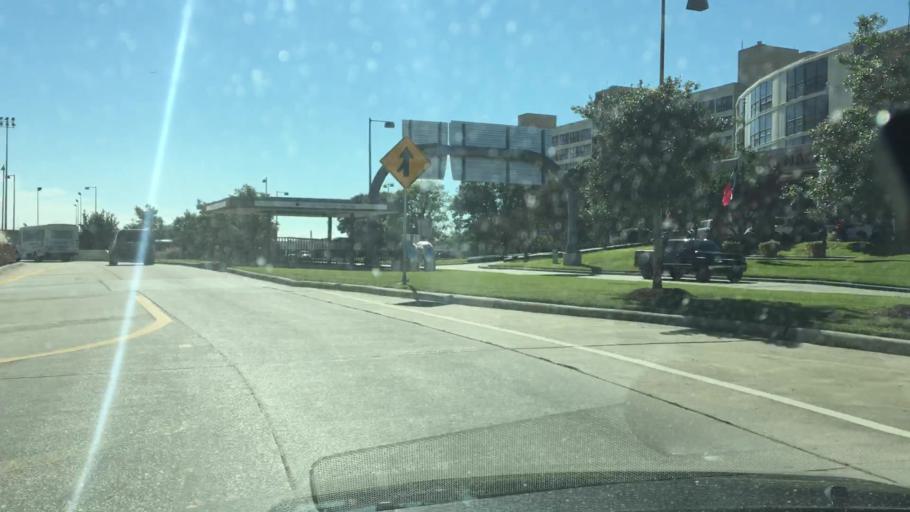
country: US
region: Texas
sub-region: Harris County
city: Aldine
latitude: 29.9870
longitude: -95.3413
